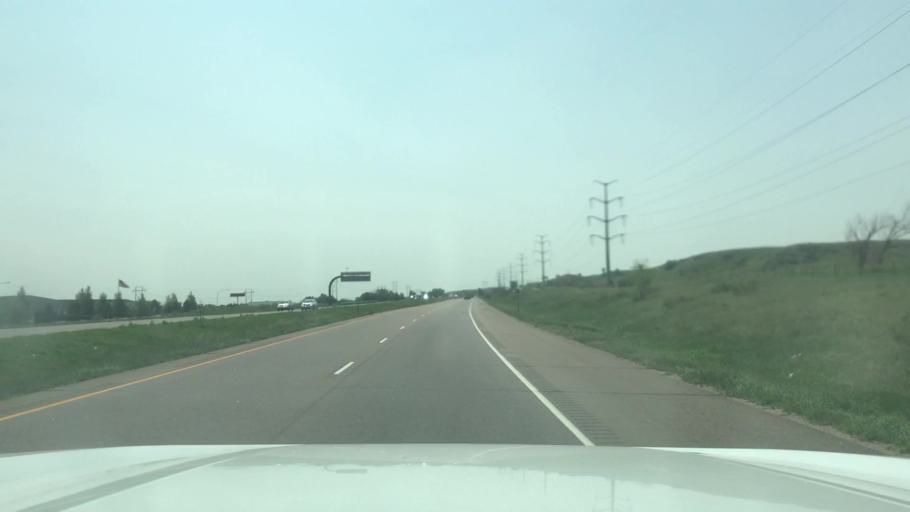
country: US
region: Colorado
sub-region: El Paso County
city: Fountain
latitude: 38.7062
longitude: -104.7235
